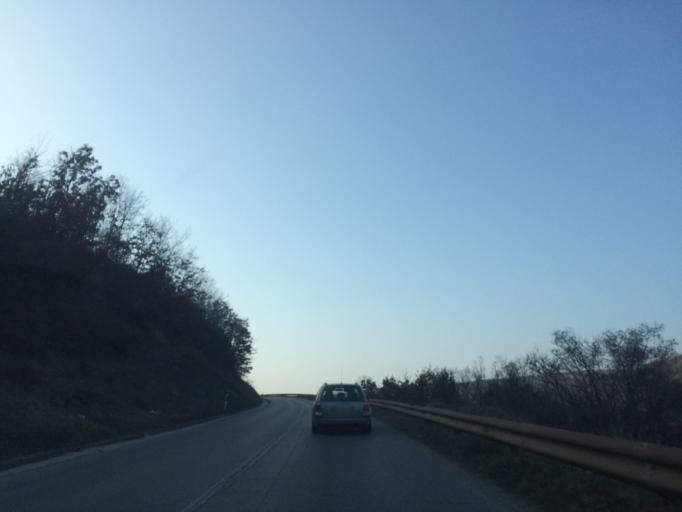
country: XK
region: Pec
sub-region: Komuna e Pejes
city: Kosuriq
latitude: 42.5045
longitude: 20.5233
